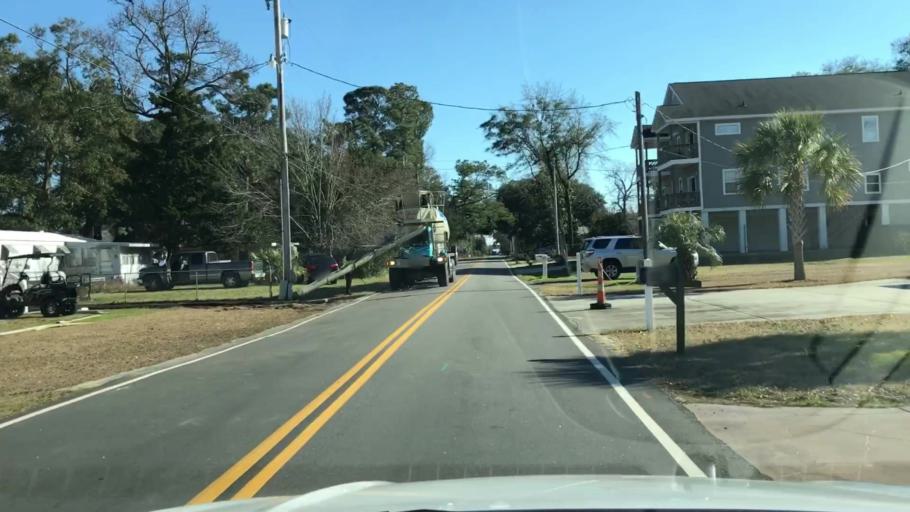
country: US
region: South Carolina
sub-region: Horry County
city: Garden City
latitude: 33.5917
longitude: -78.9983
